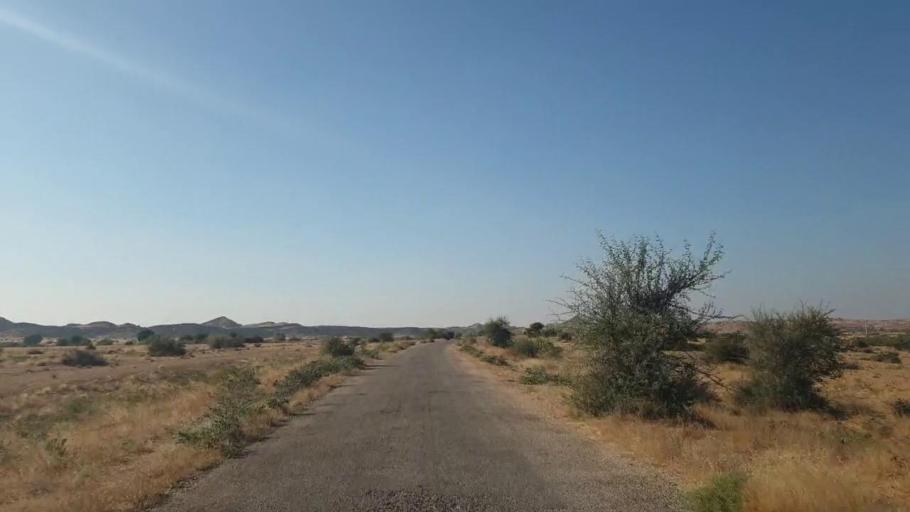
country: PK
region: Sindh
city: Malir Cantonment
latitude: 25.3928
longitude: 67.4994
